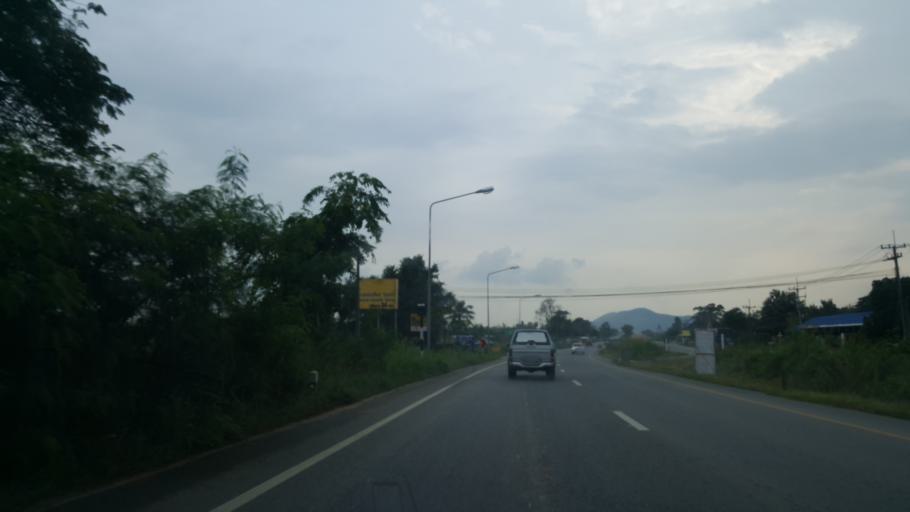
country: TH
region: Rayong
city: Ban Chang
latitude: 12.7387
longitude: 100.9900
